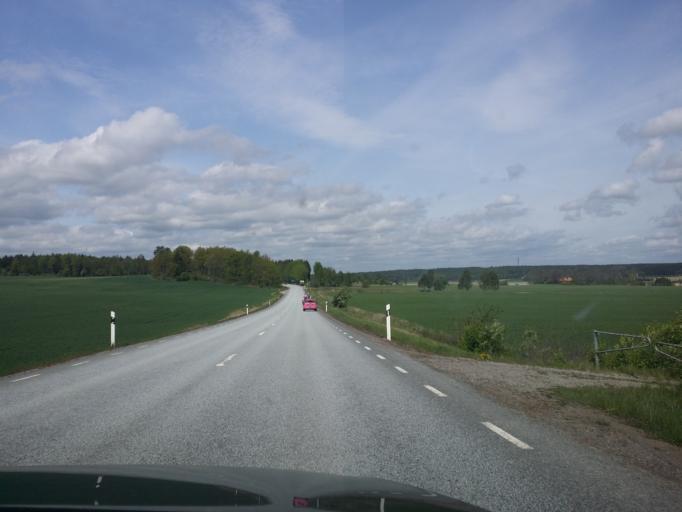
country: SE
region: Uppsala
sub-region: Habo Kommun
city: Balsta
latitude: 59.6468
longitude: 17.5654
